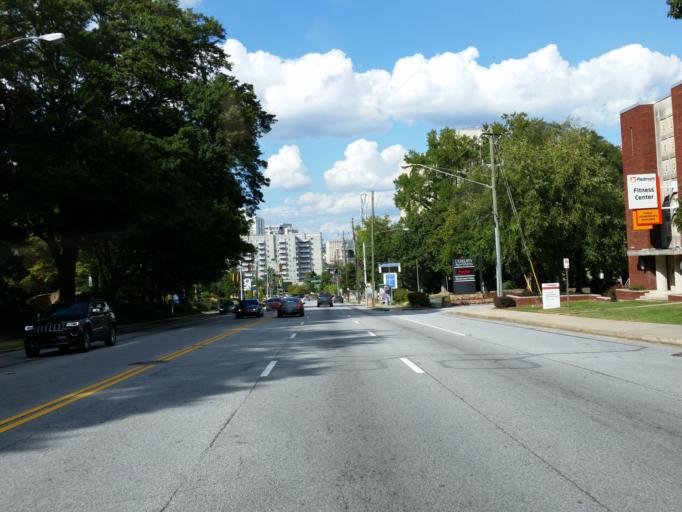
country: US
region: Georgia
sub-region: Fulton County
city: Atlanta
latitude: 33.8091
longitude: -84.3932
